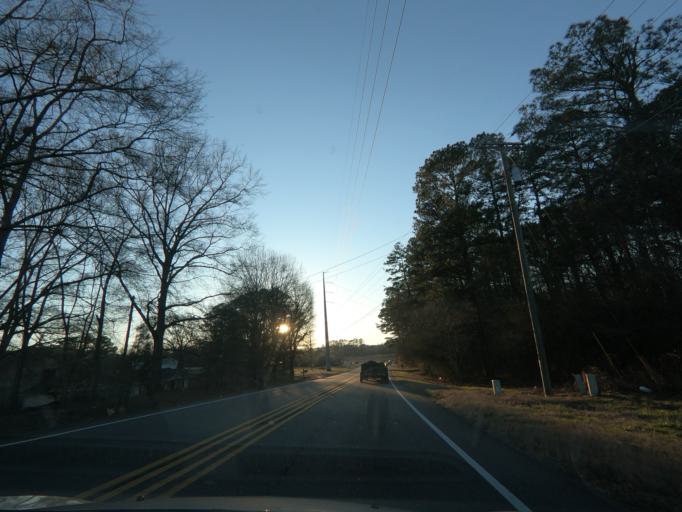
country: US
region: Georgia
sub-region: Forsyth County
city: Cumming
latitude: 34.2989
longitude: -84.1745
